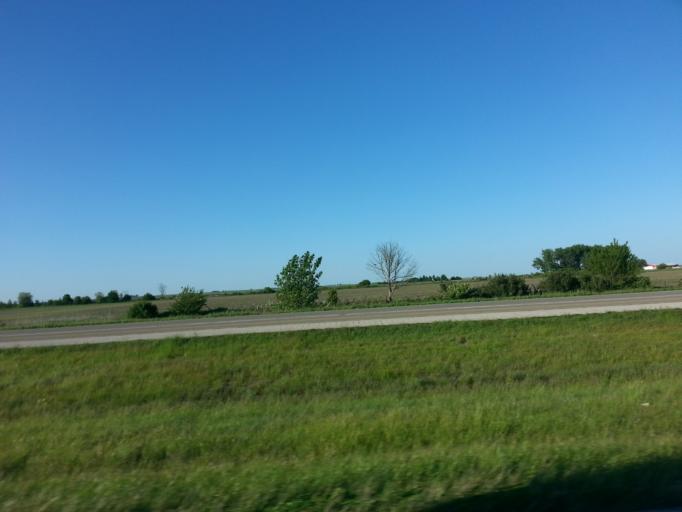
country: US
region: Illinois
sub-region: De Witt County
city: Farmer City
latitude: 40.2912
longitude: -88.6979
